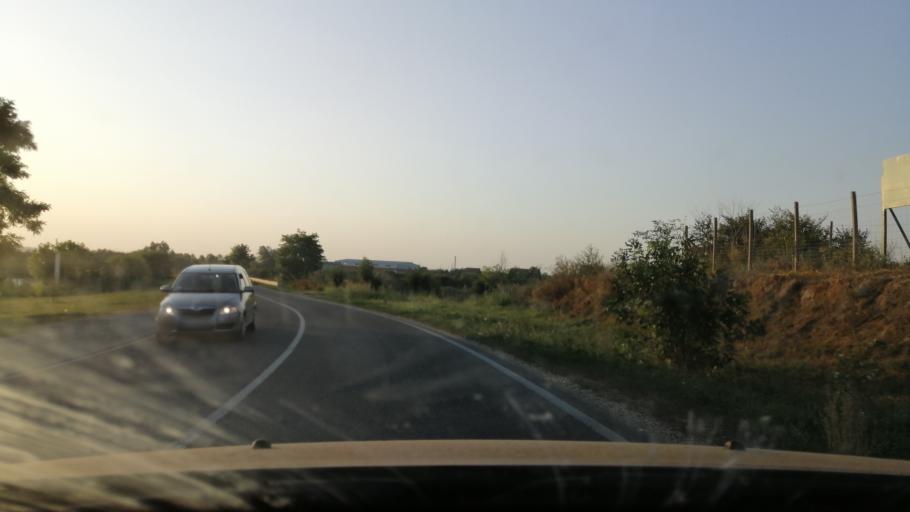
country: RS
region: Autonomna Pokrajina Vojvodina
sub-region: Juznobanatski Okrug
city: Pancevo
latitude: 44.7914
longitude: 20.7236
